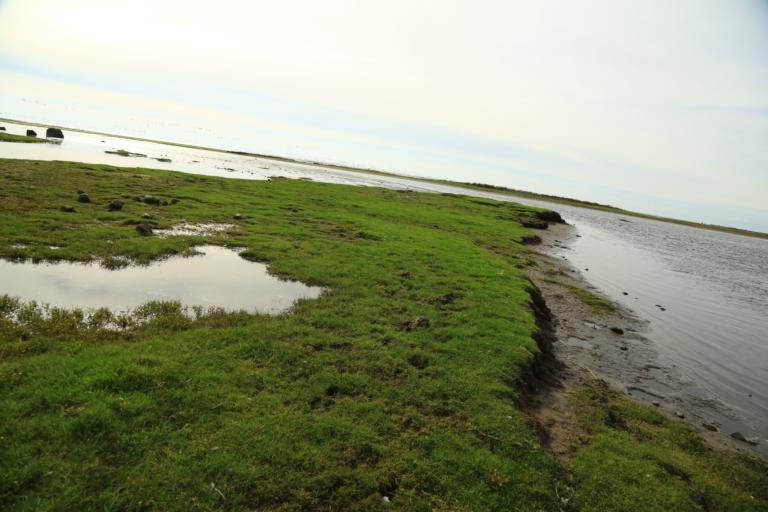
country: SE
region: Halland
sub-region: Varbergs Kommun
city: Traslovslage
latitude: 57.0234
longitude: 12.3308
